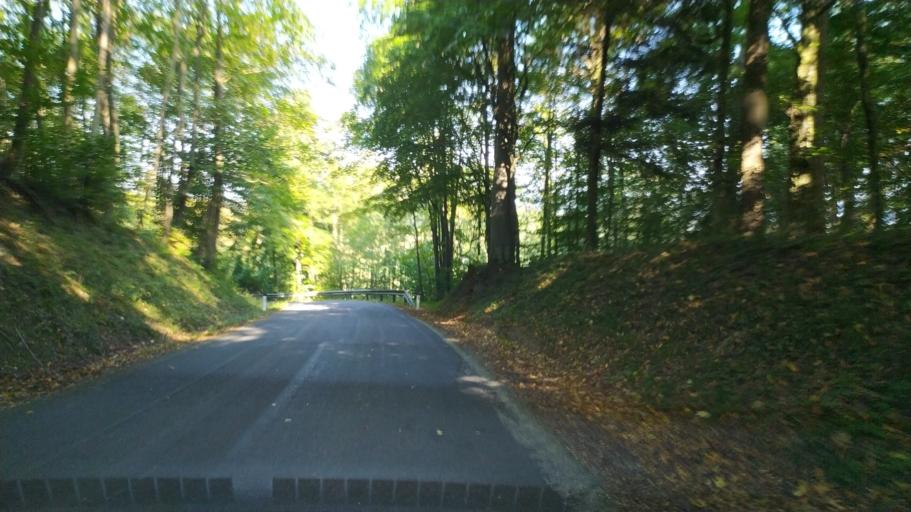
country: AT
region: Lower Austria
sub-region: Politischer Bezirk Amstetten
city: Zeillern
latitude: 48.1542
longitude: 14.7461
